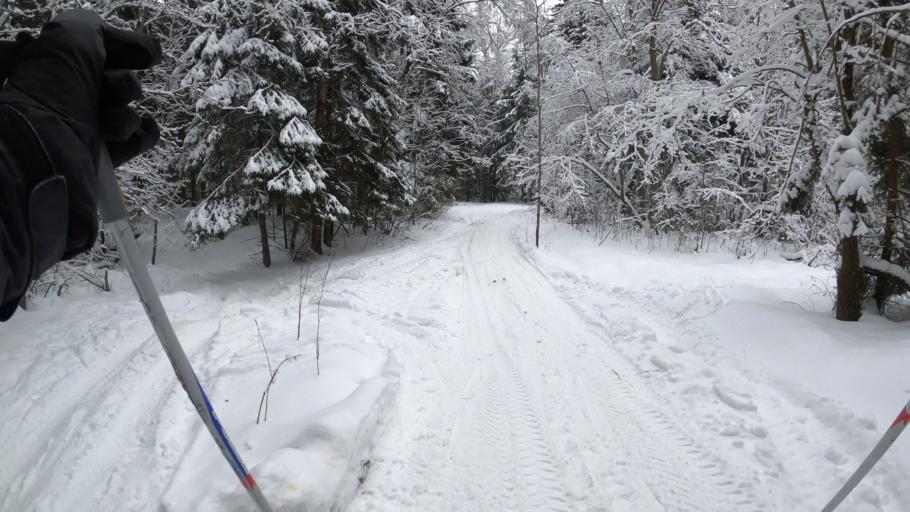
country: RU
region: Moskovskaya
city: Firsanovka
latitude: 55.9341
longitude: 37.2211
